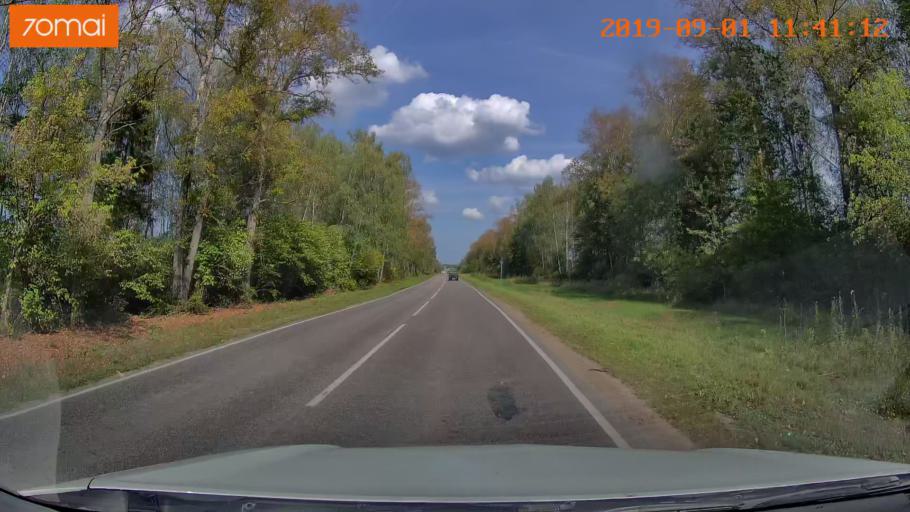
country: RU
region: Kaluga
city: Detchino
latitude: 54.8775
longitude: 36.3782
